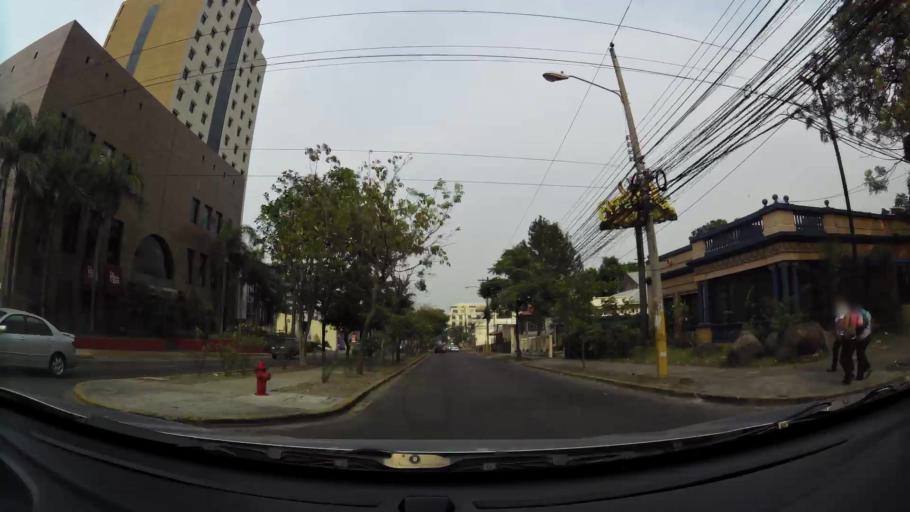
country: HN
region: Cortes
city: San Pedro Sula
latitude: 15.5063
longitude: -88.0312
